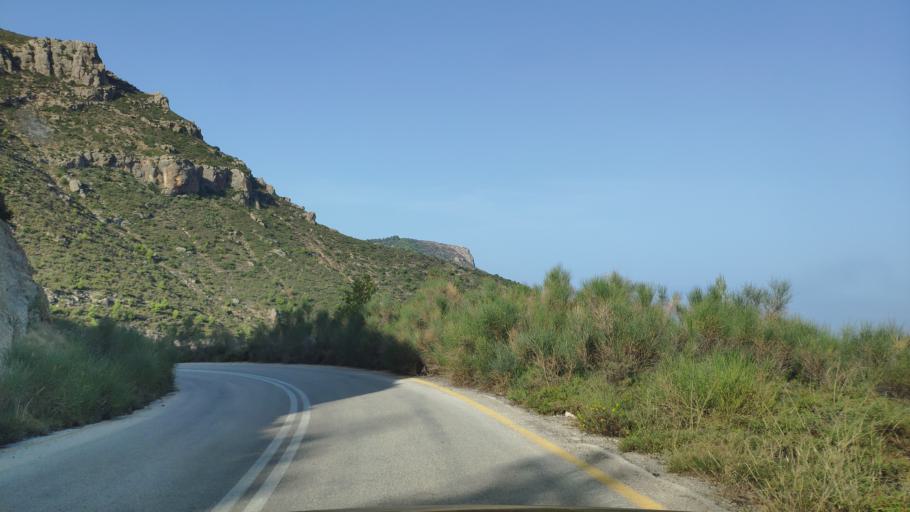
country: GR
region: West Greece
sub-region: Nomos Achaias
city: Aiyira
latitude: 38.0656
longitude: 22.3796
